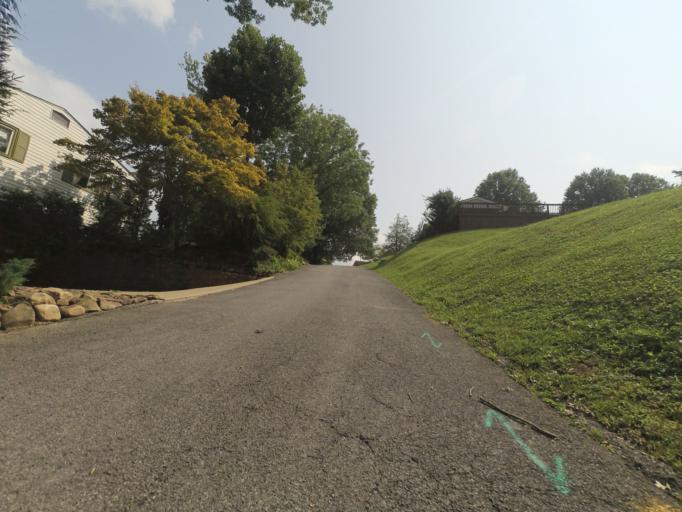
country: US
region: West Virginia
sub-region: Cabell County
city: Huntington
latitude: 38.3988
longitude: -82.4025
